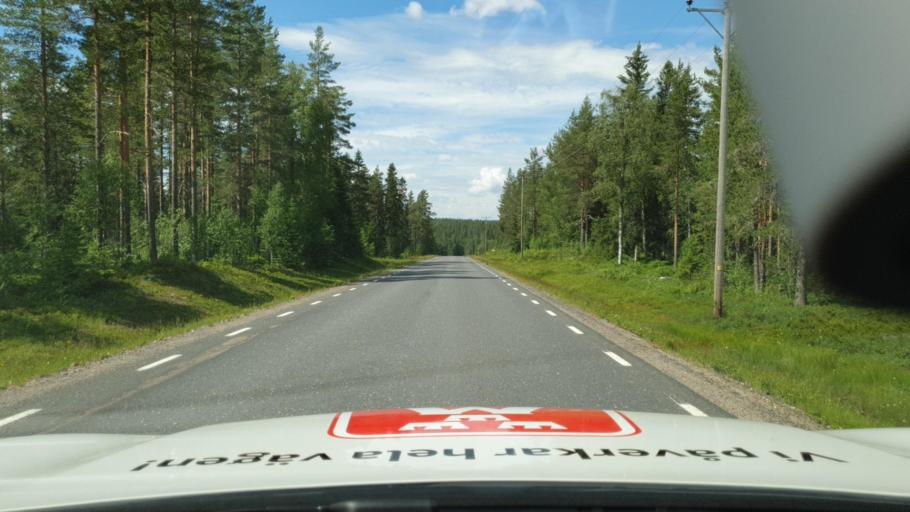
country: SE
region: Vaermland
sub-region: Torsby Kommun
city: Torsby
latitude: 60.5500
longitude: 12.7852
